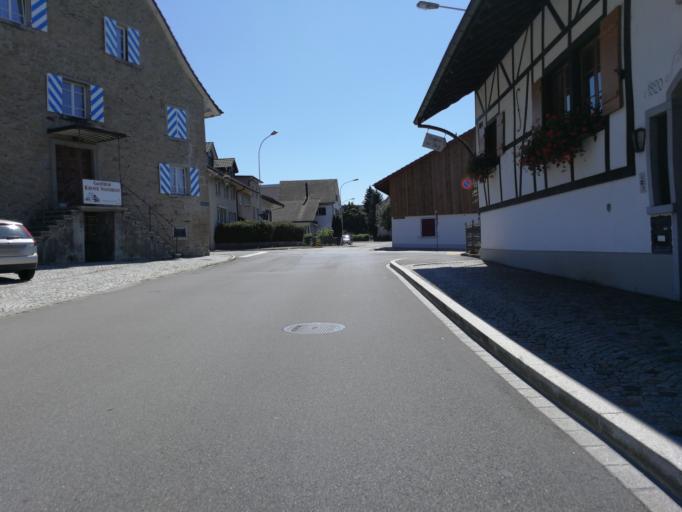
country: CH
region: Zurich
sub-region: Bezirk Uster
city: Uster / Nossikon
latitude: 47.3409
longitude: 8.7262
